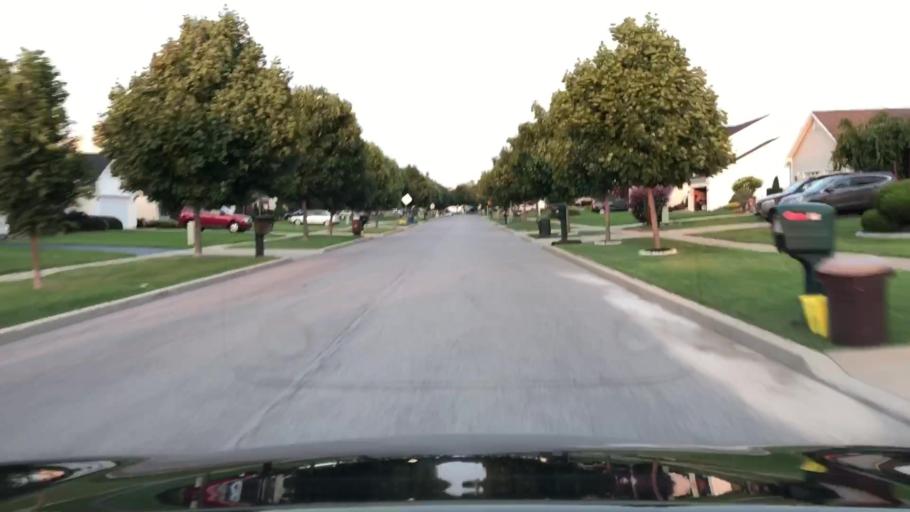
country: US
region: New York
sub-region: Erie County
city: Lancaster
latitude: 42.8663
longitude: -78.6834
